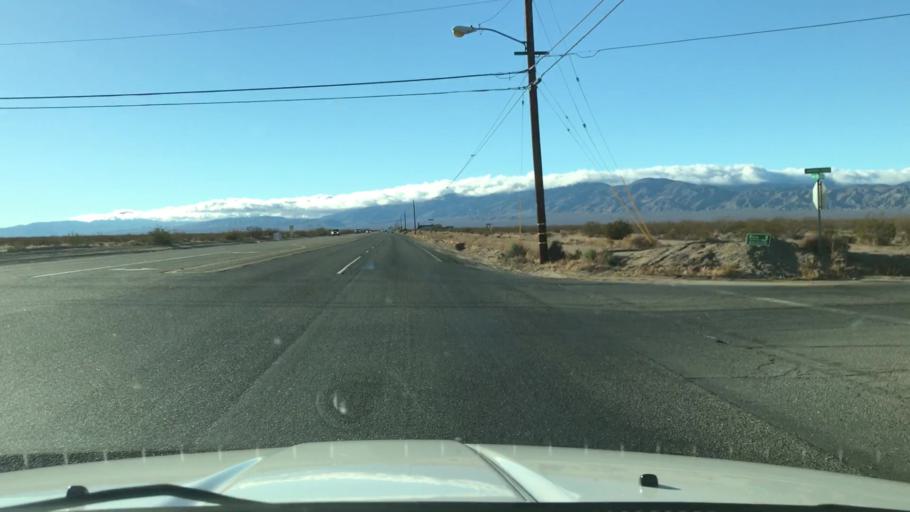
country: US
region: California
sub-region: Kern County
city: California City
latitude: 35.1253
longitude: -118.0142
